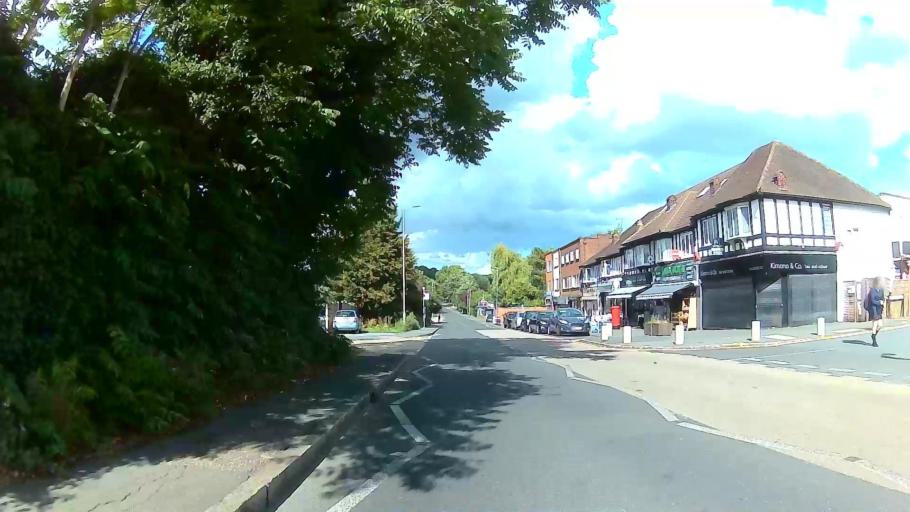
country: GB
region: England
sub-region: Essex
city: Grange Hill
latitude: 51.6130
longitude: 0.0903
